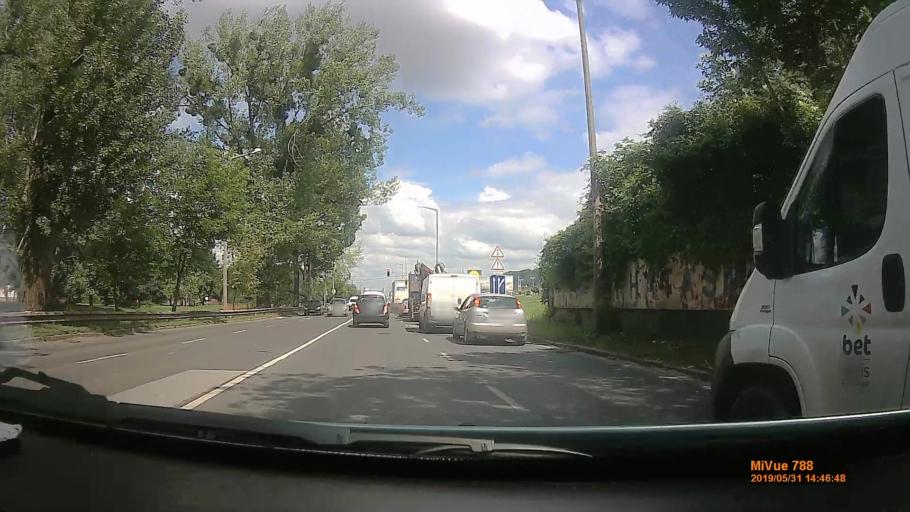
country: HU
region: Borsod-Abauj-Zemplen
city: Sajobabony
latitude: 48.1217
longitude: 20.7178
